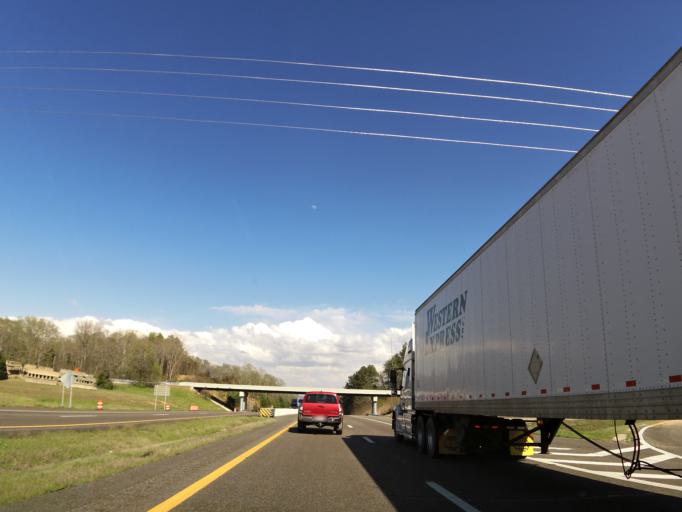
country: US
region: Tennessee
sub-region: Humphreys County
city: New Johnsonville
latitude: 35.8686
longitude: -87.9717
